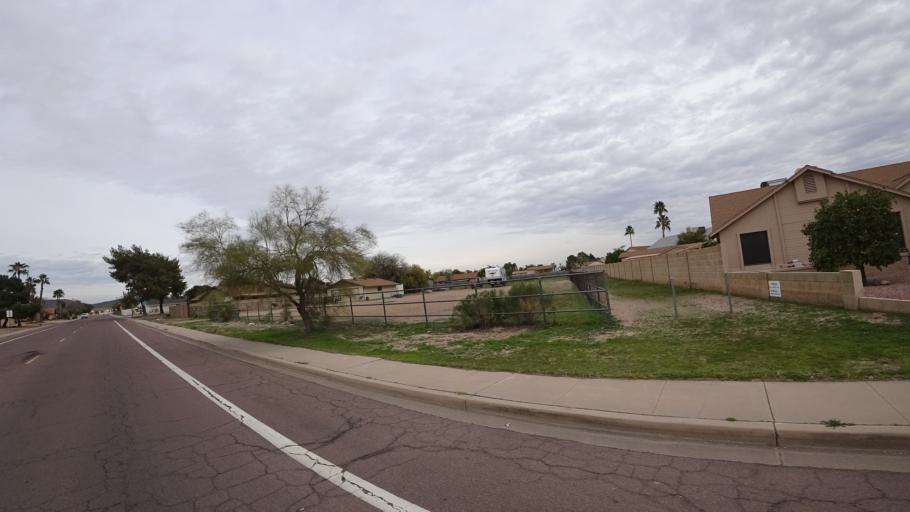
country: US
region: Arizona
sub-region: Maricopa County
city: Peoria
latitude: 33.6460
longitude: -112.1940
